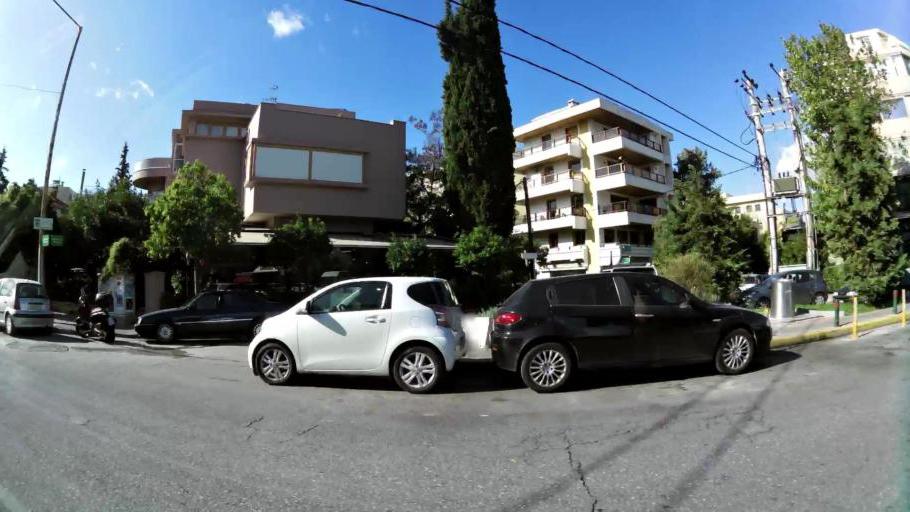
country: GR
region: Attica
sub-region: Nomarchia Athinas
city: Neo Psychiko
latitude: 38.0031
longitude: 23.7762
